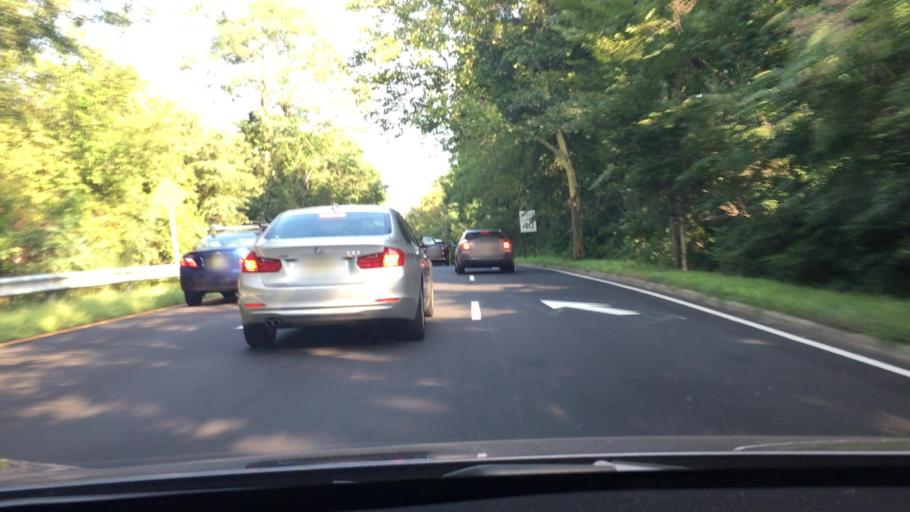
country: US
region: New York
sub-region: Nassau County
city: Old Westbury
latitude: 40.7797
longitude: -73.5809
